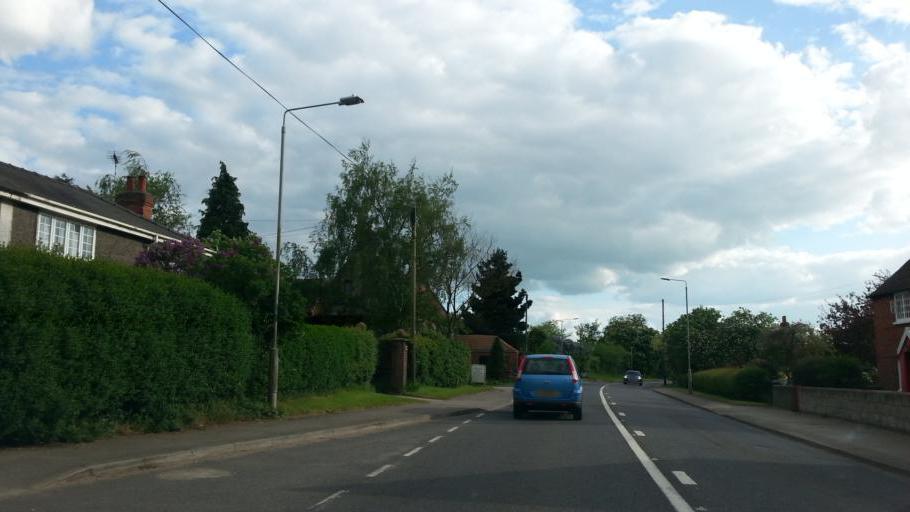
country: GB
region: England
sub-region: Nottinghamshire
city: South Collingham
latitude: 53.1161
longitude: -0.7727
